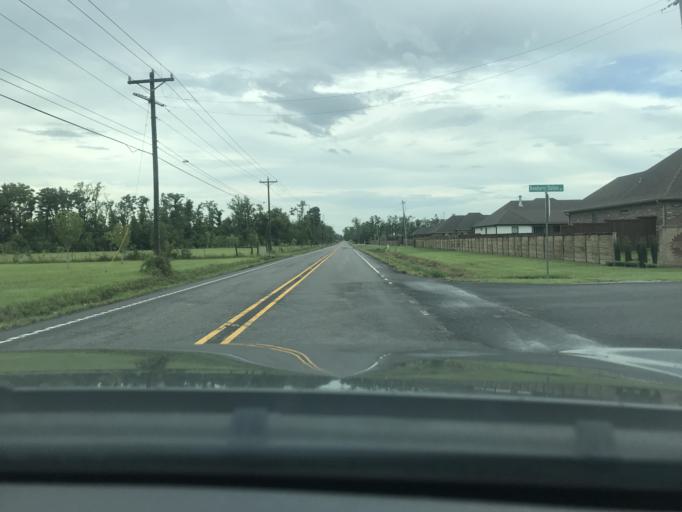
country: US
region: Louisiana
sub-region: Calcasieu Parish
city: Westlake
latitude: 30.3092
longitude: -93.2584
